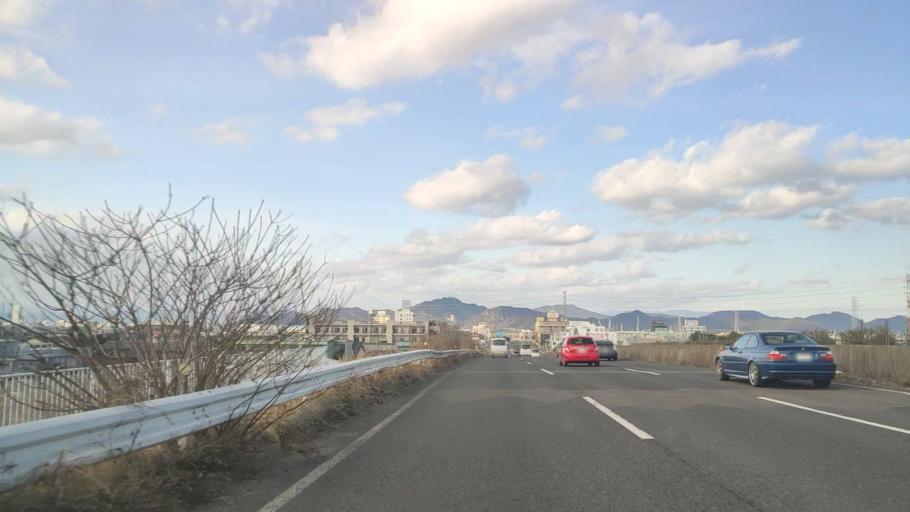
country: JP
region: Gifu
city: Kasamatsucho
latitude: 35.3748
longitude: 136.7840
